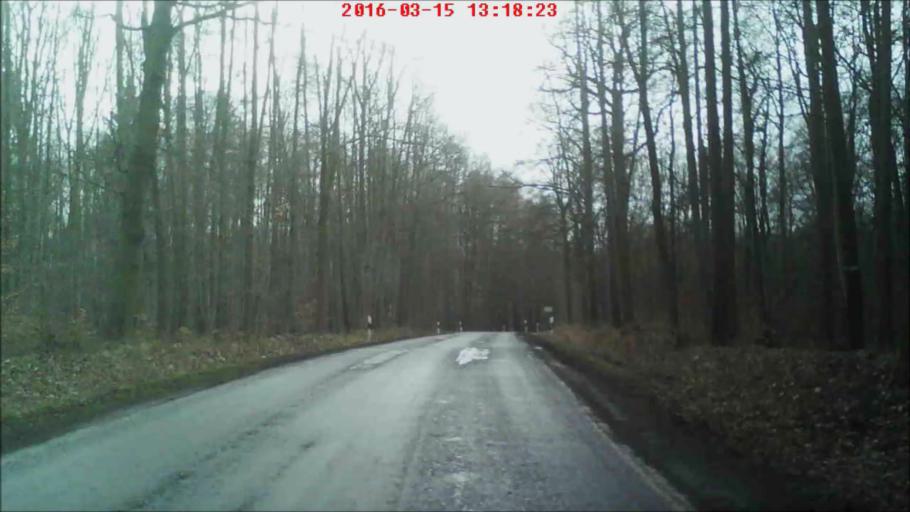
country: DE
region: Thuringia
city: Erfurt
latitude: 50.9410
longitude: 11.0319
